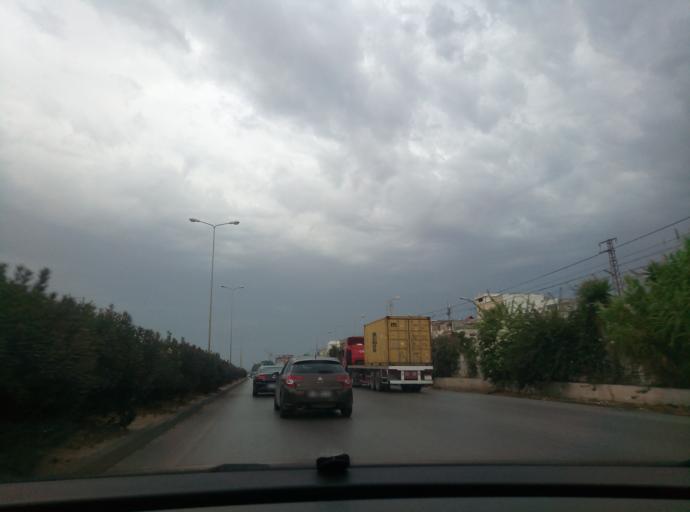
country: TN
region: Bin 'Arus
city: Ben Arous
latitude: 36.7522
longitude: 10.2044
